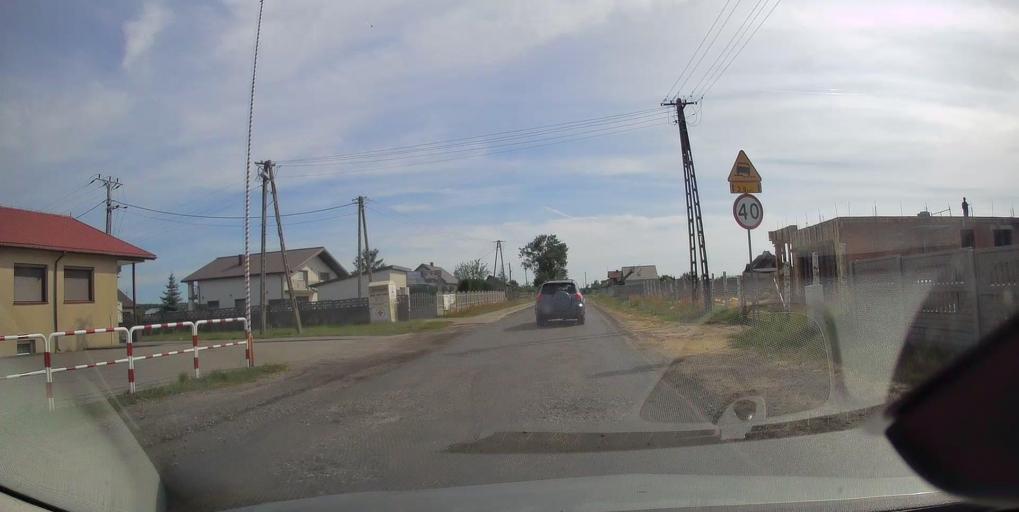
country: PL
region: Lodz Voivodeship
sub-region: Powiat tomaszowski
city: Tomaszow Mazowiecki
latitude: 51.4544
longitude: 20.0347
